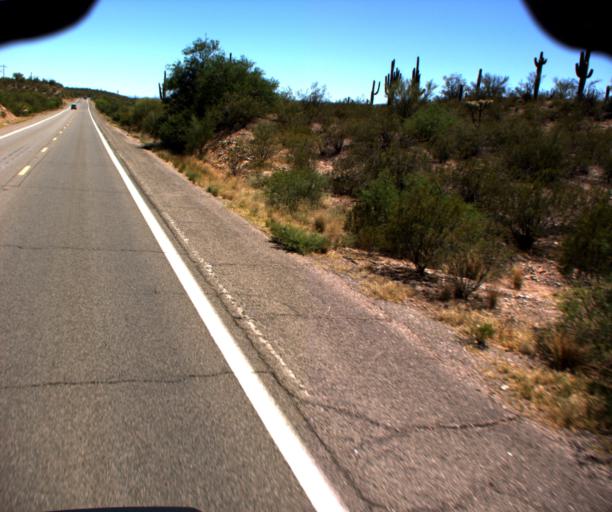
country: US
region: Arizona
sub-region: Pinal County
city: Mammoth
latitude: 32.8645
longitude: -110.7097
